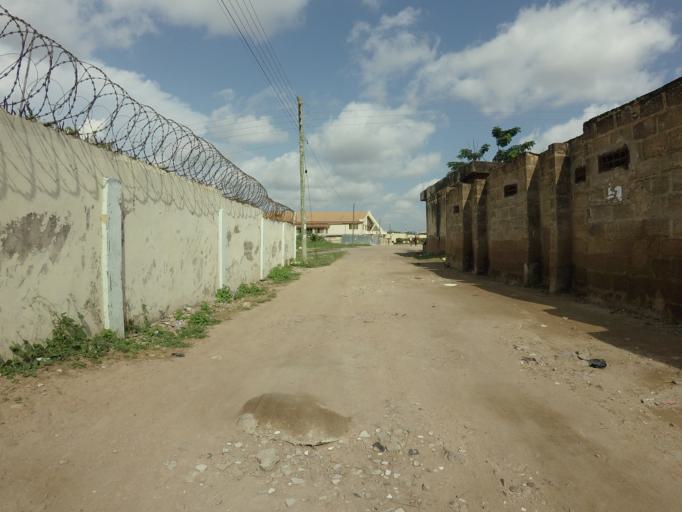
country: GH
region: Greater Accra
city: Dome
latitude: 5.6185
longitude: -0.2380
